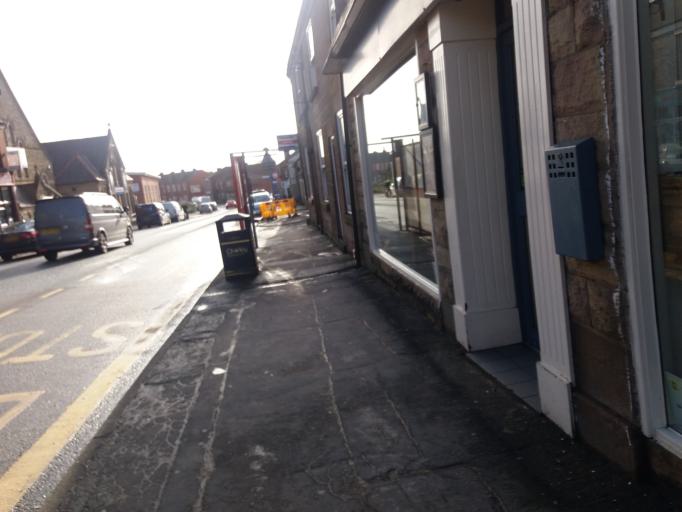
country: GB
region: England
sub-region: Lancashire
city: Adlington
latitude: 53.6115
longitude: -2.6050
